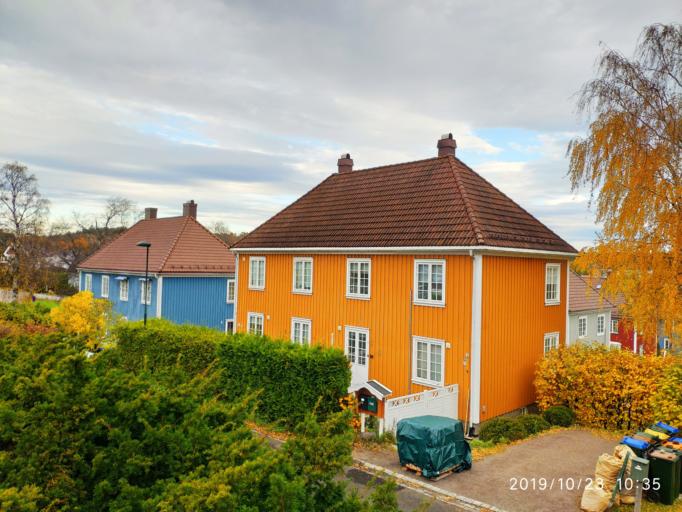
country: NO
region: Vestfold
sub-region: Tonsberg
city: Tonsberg
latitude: 59.2735
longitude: 10.4172
